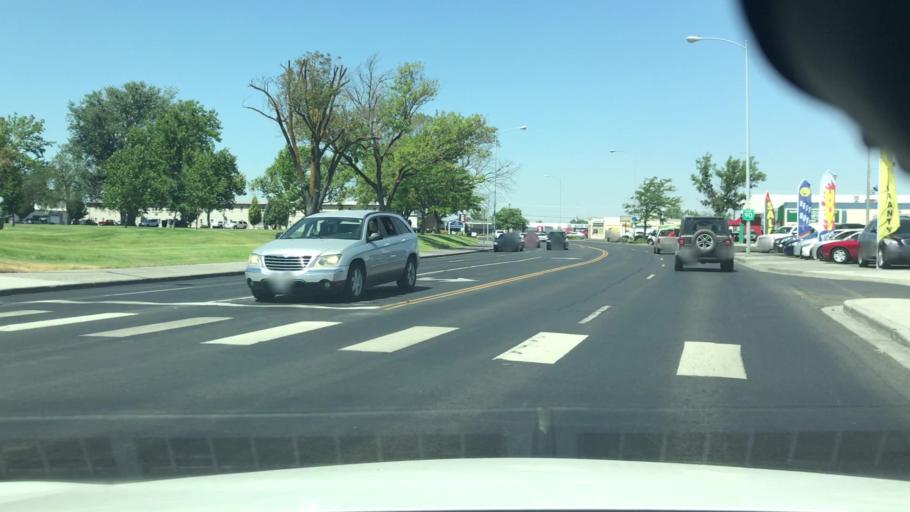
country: US
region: Washington
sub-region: Grant County
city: Moses Lake
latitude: 47.1313
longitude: -119.2706
